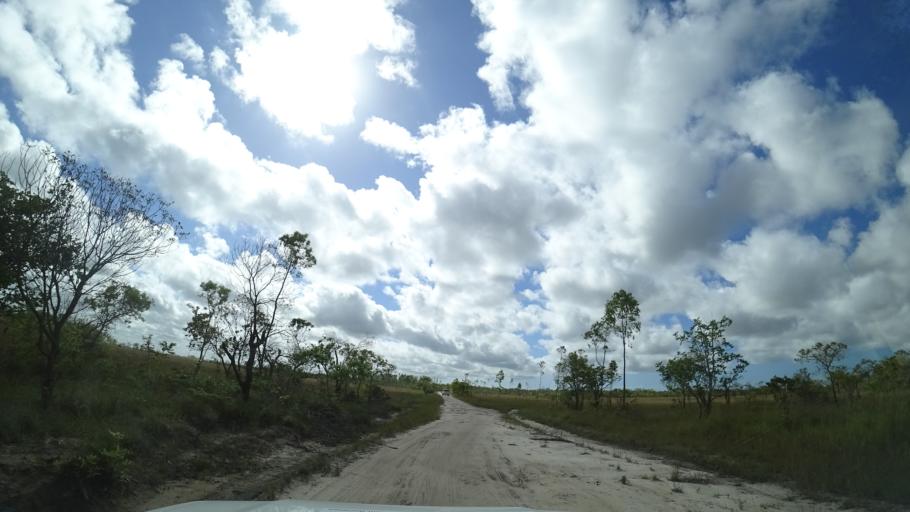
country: MZ
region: Sofala
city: Beira
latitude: -19.6122
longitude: 35.0767
